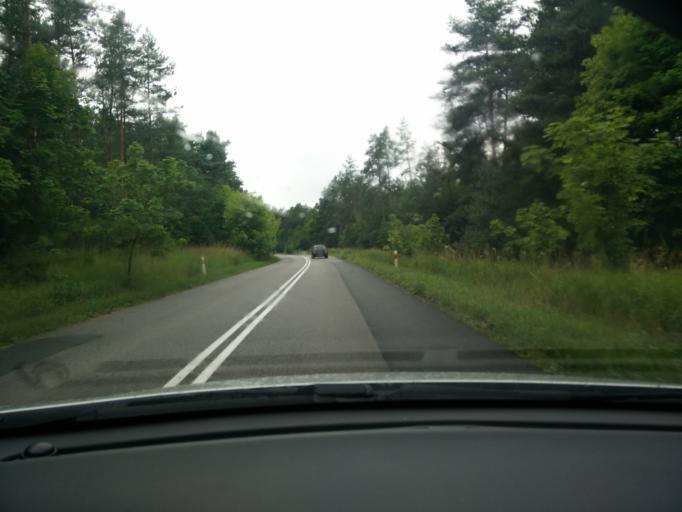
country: PL
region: Pomeranian Voivodeship
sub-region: Powiat pucki
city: Kosakowo
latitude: 54.6042
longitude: 18.4769
